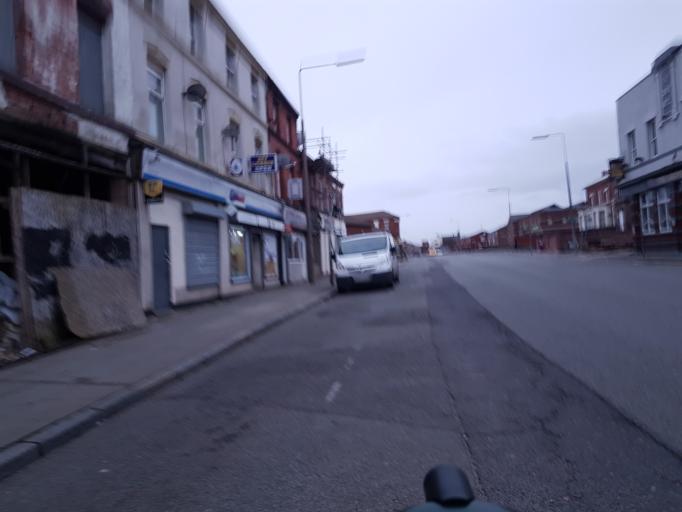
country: GB
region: England
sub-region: Liverpool
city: Liverpool
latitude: 53.4255
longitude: -2.9646
